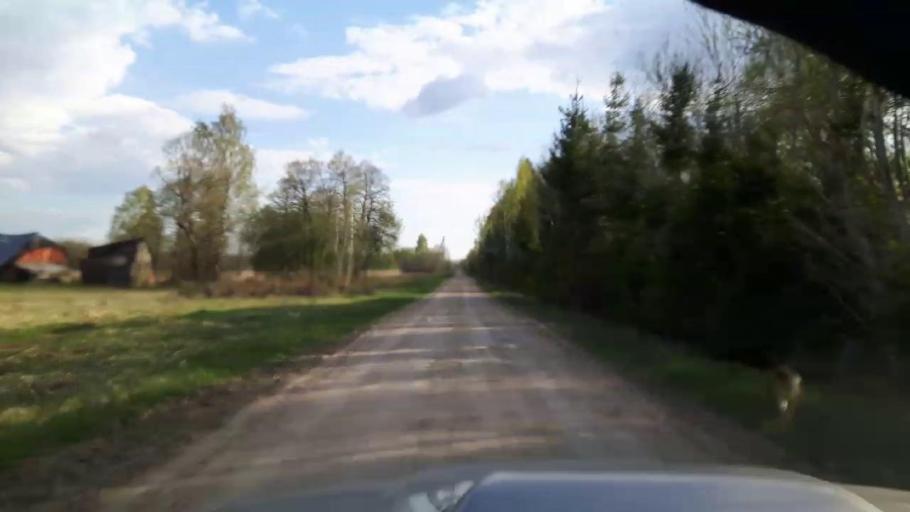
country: EE
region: Paernumaa
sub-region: Tootsi vald
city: Tootsi
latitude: 58.4368
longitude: 24.8089
